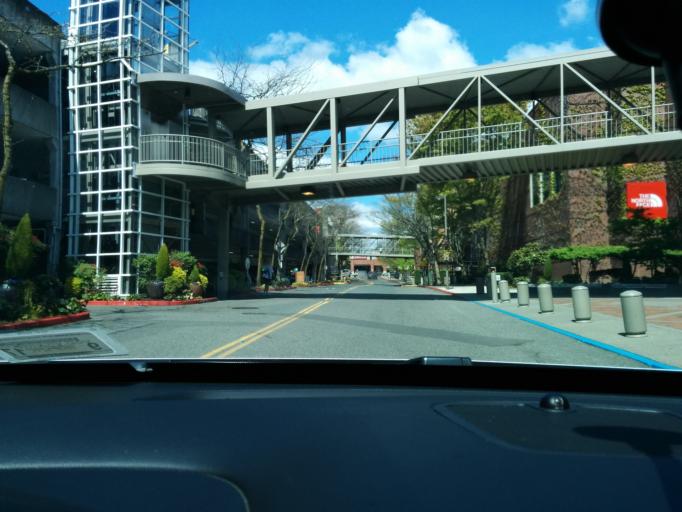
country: US
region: Washington
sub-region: King County
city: Bellevue
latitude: 47.6159
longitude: -122.2053
